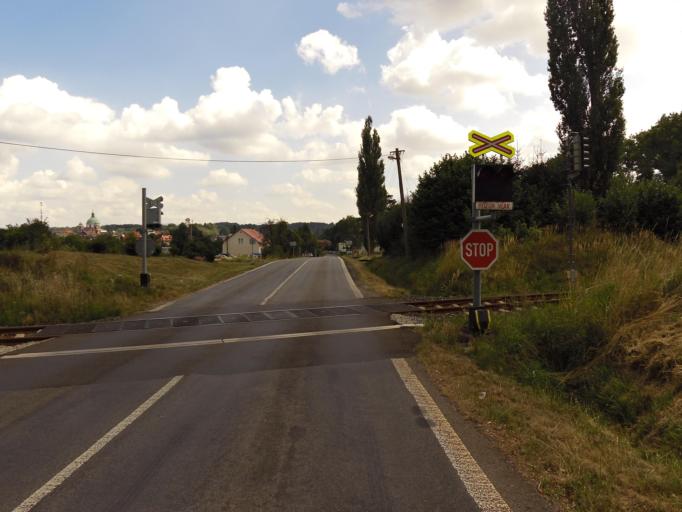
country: CZ
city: Jablonne v Podjestedi
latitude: 50.7662
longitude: 14.7504
